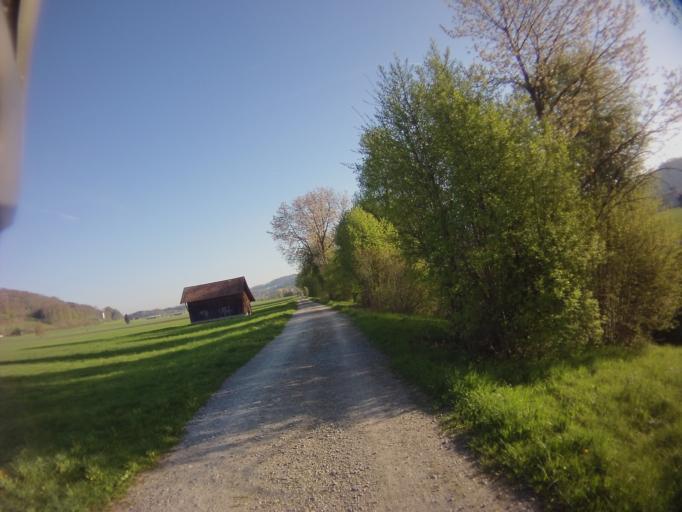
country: CH
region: Zurich
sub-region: Bezirk Affoltern
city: Schachen
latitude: 47.3230
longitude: 8.4644
